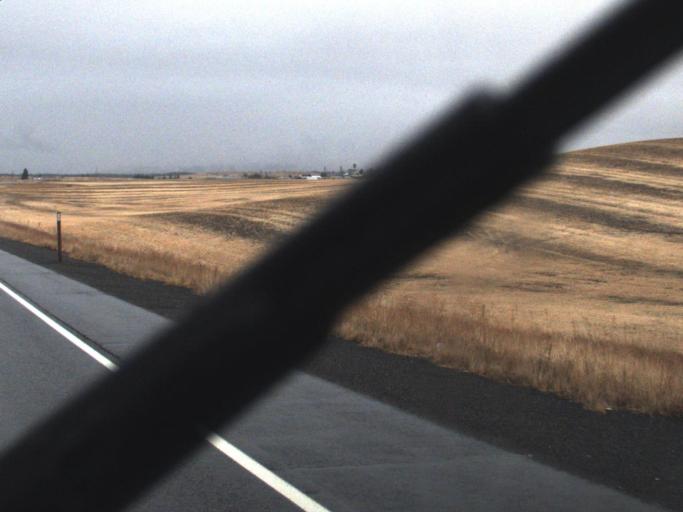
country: US
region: Washington
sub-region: Spokane County
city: Cheney
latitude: 47.4130
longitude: -117.3917
